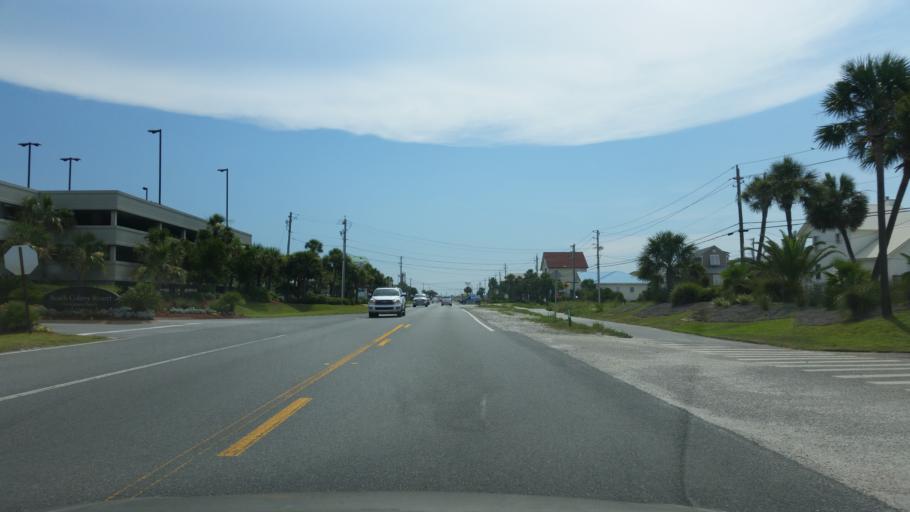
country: US
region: Florida
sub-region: Santa Rosa County
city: Navarre
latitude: 30.3809
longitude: -86.8672
